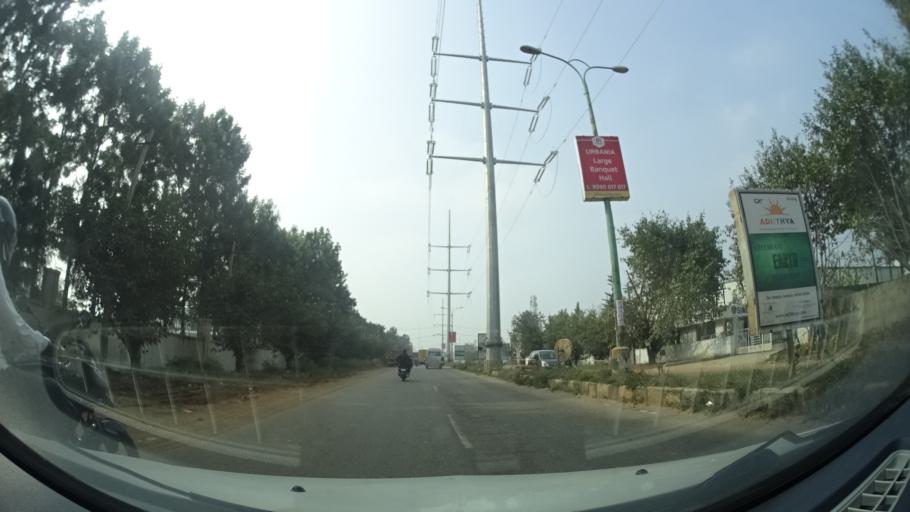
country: IN
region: Karnataka
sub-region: Bangalore Urban
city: Anekal
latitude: 12.7967
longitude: 77.6604
